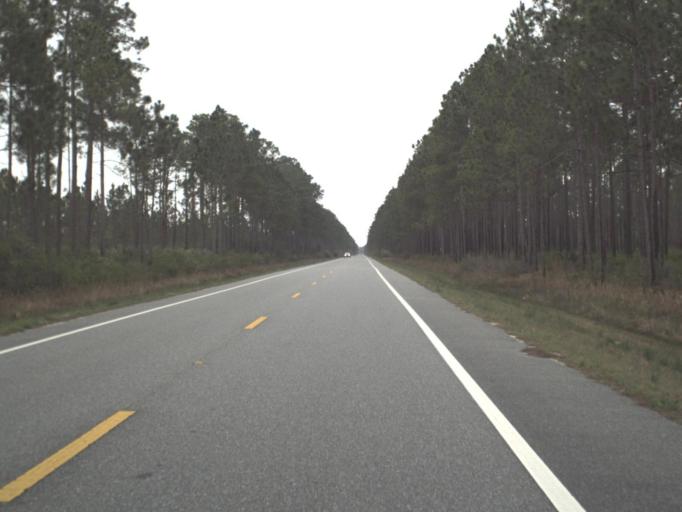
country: US
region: Florida
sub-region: Franklin County
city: Apalachicola
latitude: 29.8831
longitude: -84.9765
